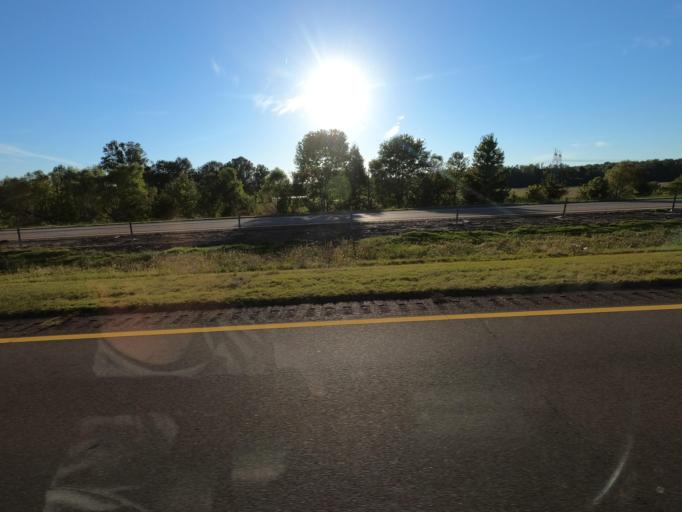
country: US
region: Tennessee
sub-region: Shelby County
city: Arlington
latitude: 35.3022
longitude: -89.6962
